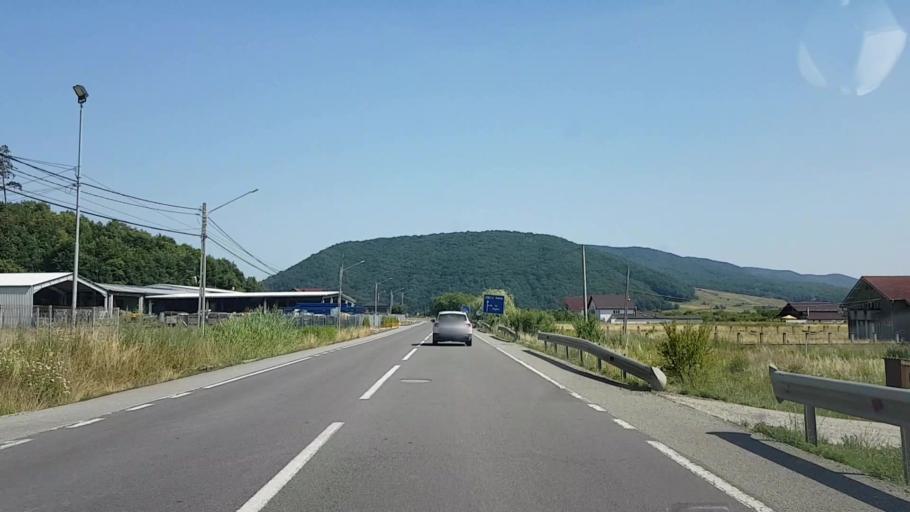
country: RO
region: Bistrita-Nasaud
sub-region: Comuna Sieu-Magherus
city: Sieu-Magherus
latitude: 47.0661
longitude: 24.4123
